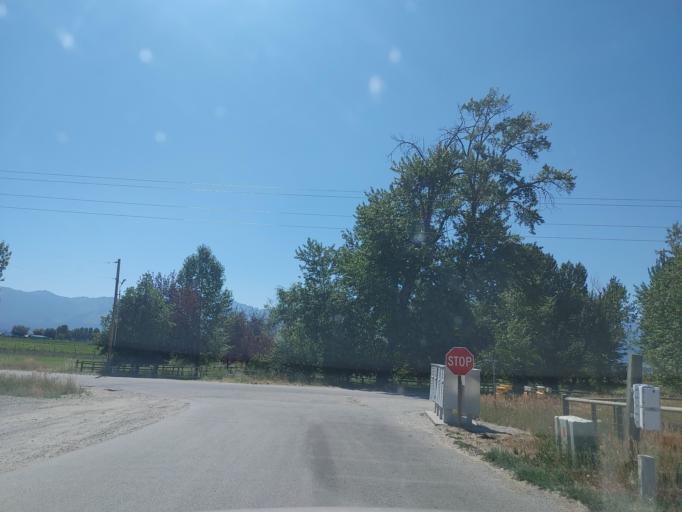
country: US
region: Montana
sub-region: Ravalli County
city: Hamilton
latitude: 46.3482
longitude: -114.0611
